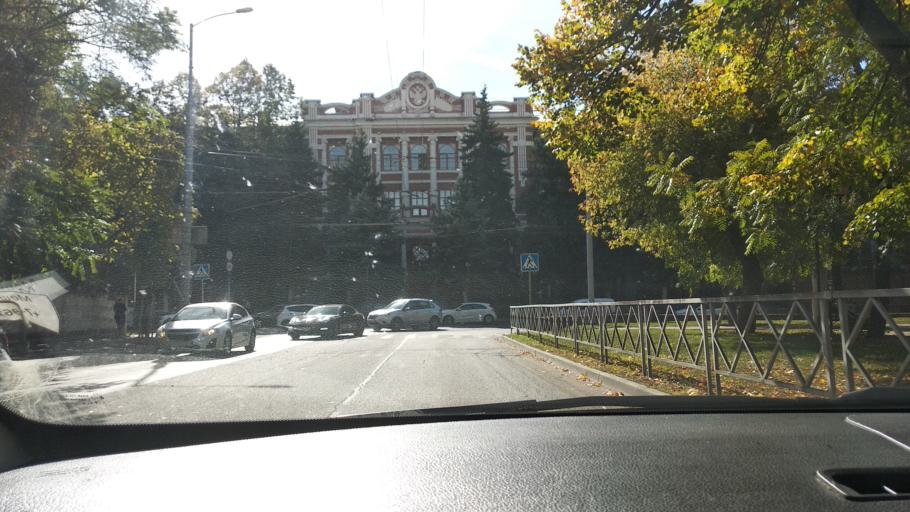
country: RU
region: Adygeya
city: Yablonovskiy
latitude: 45.0136
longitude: 38.9622
